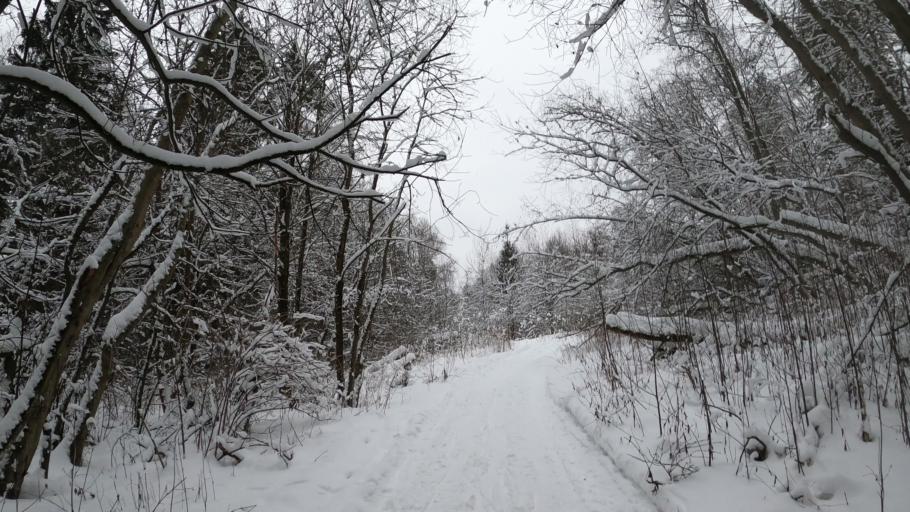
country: RU
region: Moskovskaya
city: Firsanovka
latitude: 55.9367
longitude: 37.2183
